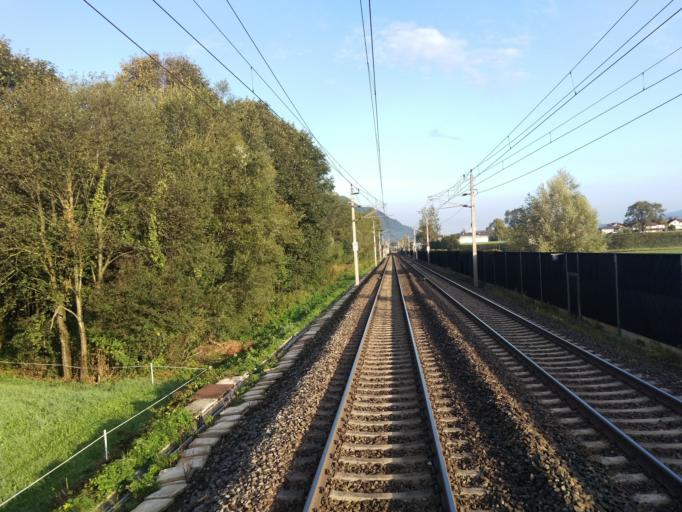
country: AT
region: Salzburg
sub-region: Politischer Bezirk Hallein
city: Kuchl
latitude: 47.6181
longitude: 13.1486
